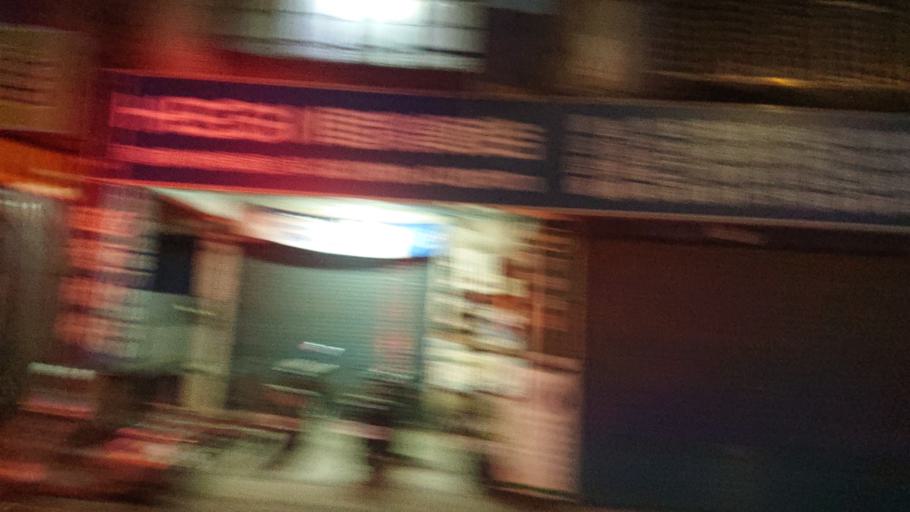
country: TW
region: Taipei
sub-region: Taipei
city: Banqiao
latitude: 24.9639
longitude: 121.4270
